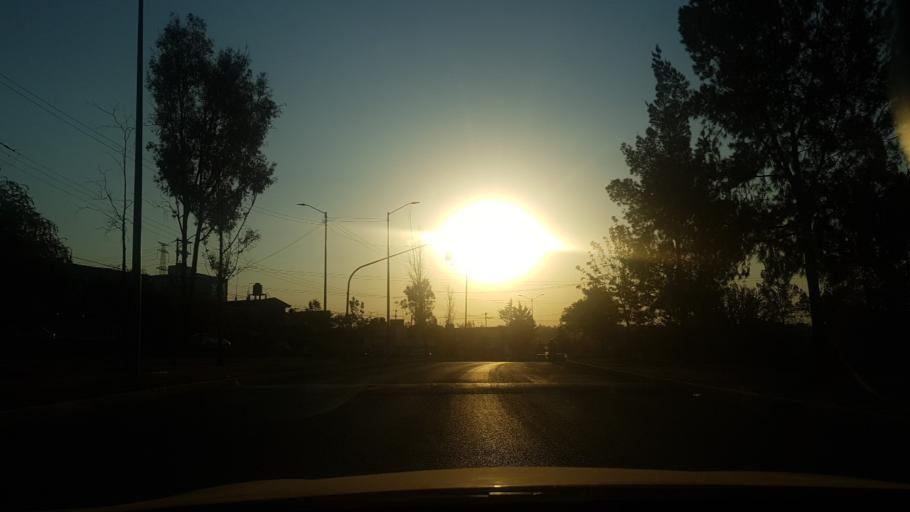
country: MX
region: Mexico
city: Cuautitlan Izcalli
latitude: 19.6365
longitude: -99.2163
